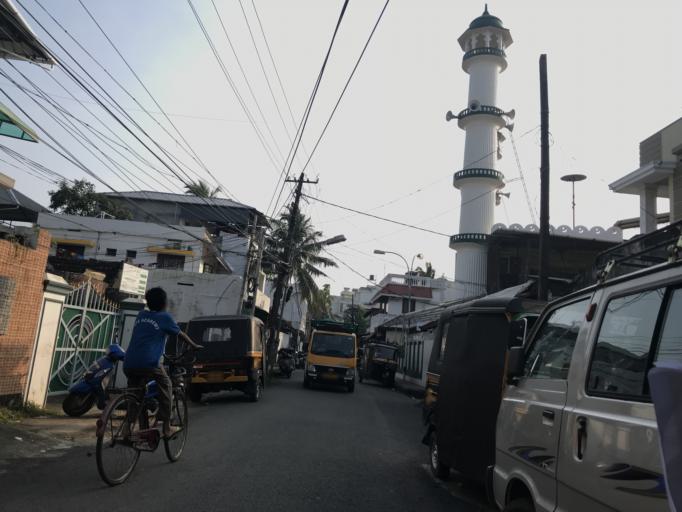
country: IN
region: Kerala
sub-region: Ernakulam
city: Cochin
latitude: 9.9646
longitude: 76.2478
